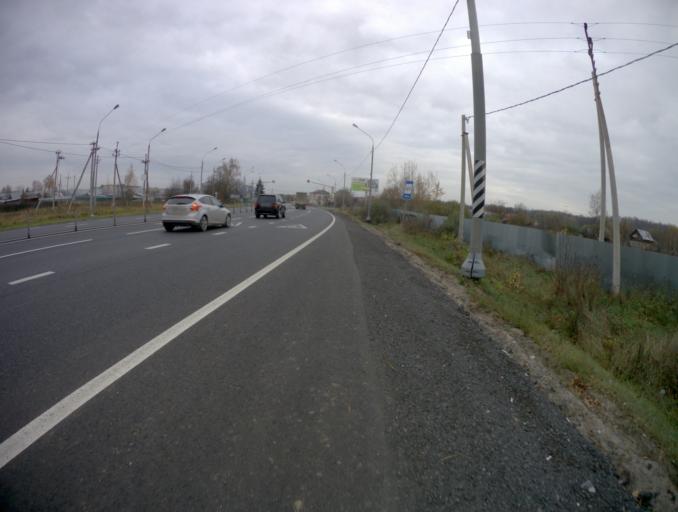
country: RU
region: Moskovskaya
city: Malaya Dubna
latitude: 55.8744
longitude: 38.9636
